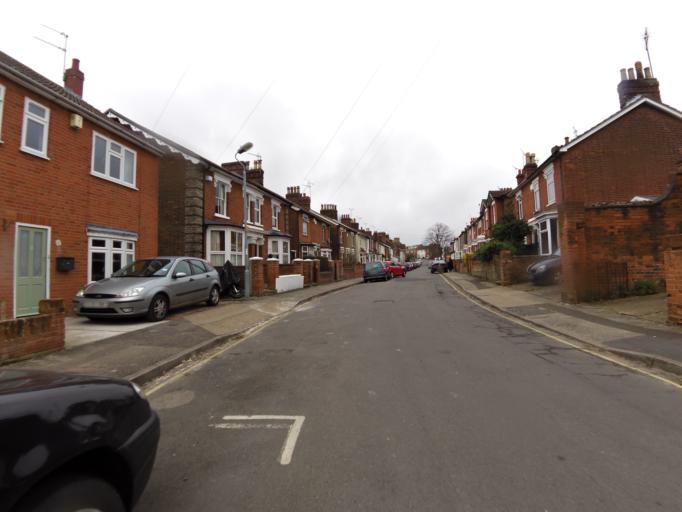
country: GB
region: England
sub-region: Suffolk
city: Ipswich
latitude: 52.0590
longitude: 1.1651
